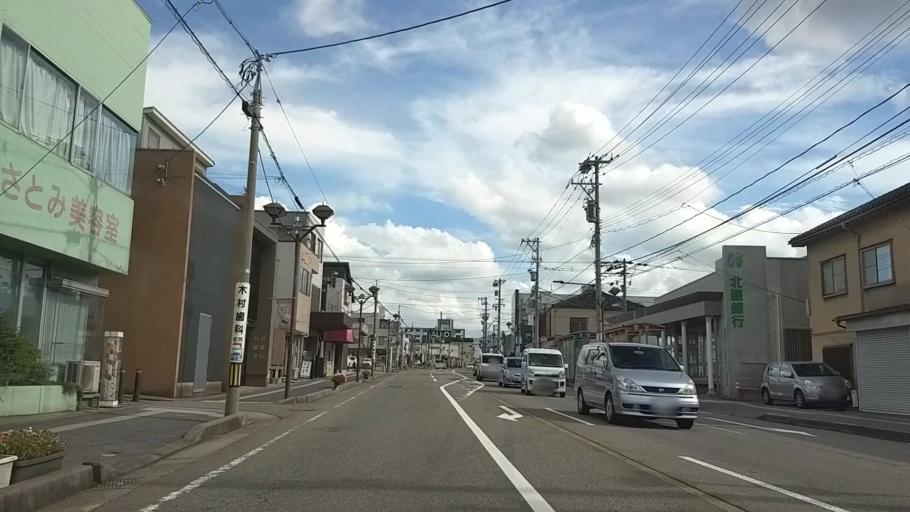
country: JP
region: Ishikawa
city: Nonoichi
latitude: 36.5425
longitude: 136.6630
